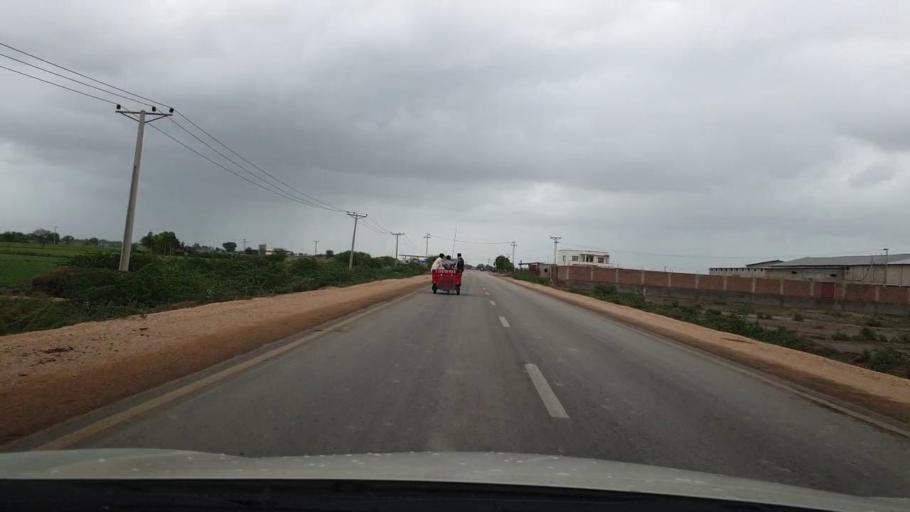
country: PK
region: Sindh
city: Badin
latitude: 24.6526
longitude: 68.7715
